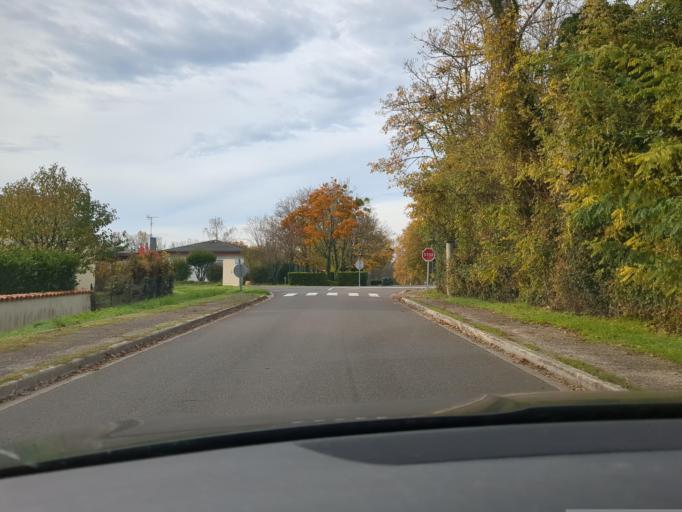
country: FR
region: Poitou-Charentes
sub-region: Departement de la Charente-Maritime
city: Jonzac
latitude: 45.4512
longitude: -0.4469
